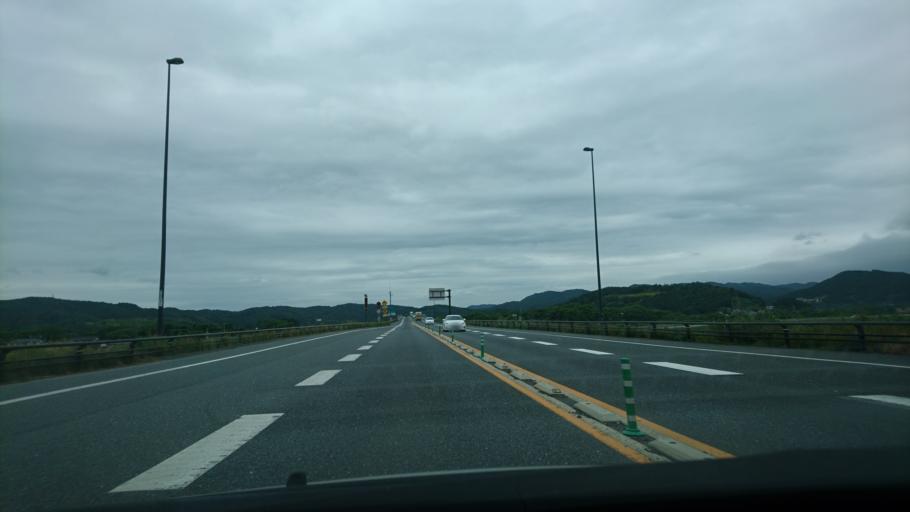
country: JP
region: Miyagi
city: Wakuya
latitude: 38.6001
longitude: 141.2826
